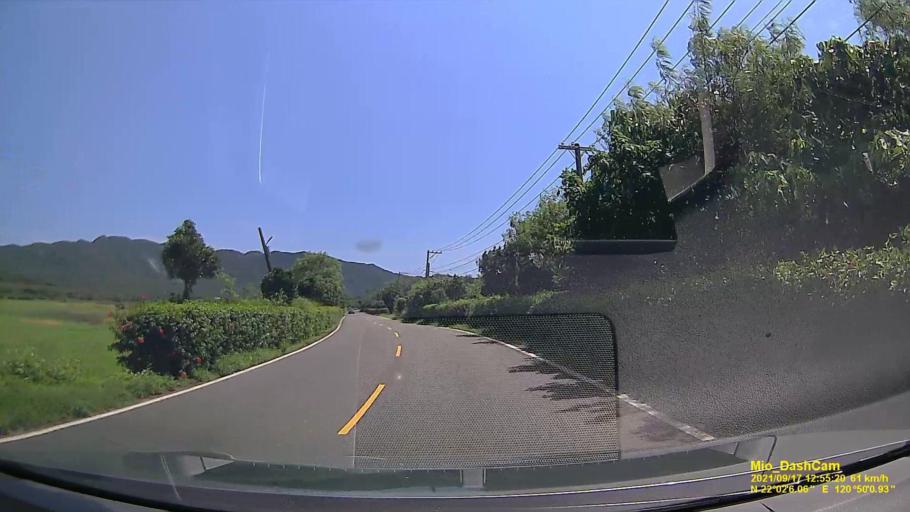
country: TW
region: Taiwan
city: Hengchun
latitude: 22.0349
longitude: 120.8336
